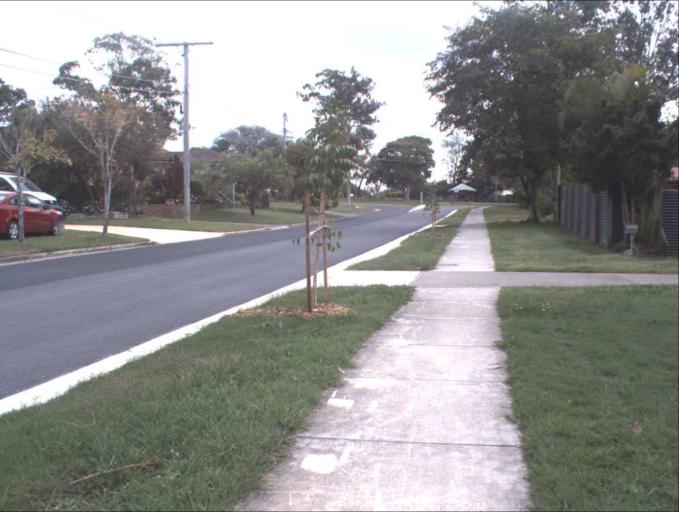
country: AU
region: Queensland
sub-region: Brisbane
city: Sunnybank Hills
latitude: -27.6587
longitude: 153.0510
